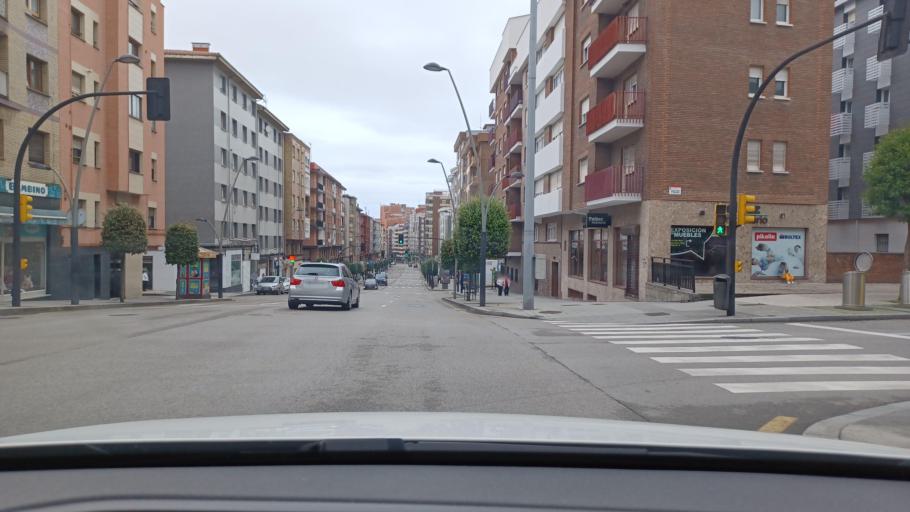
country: ES
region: Asturias
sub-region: Province of Asturias
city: Gijon
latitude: 43.5320
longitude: -5.6542
